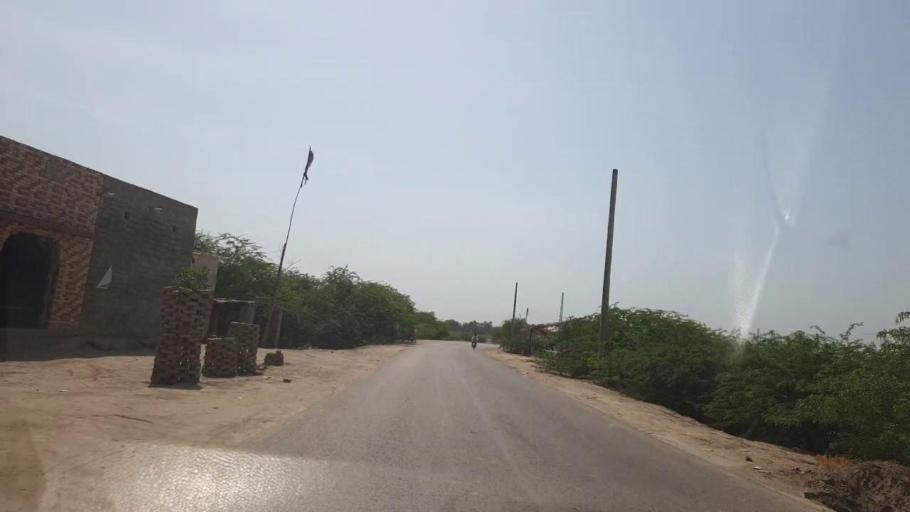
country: PK
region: Sindh
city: Bozdar
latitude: 27.1231
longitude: 68.5434
